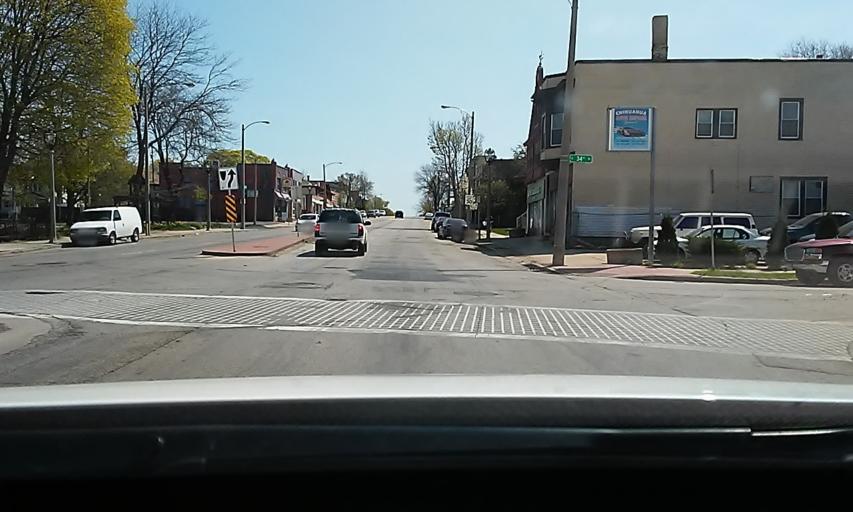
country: US
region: Wisconsin
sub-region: Milwaukee County
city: West Milwaukee
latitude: 43.0216
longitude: -87.9567
